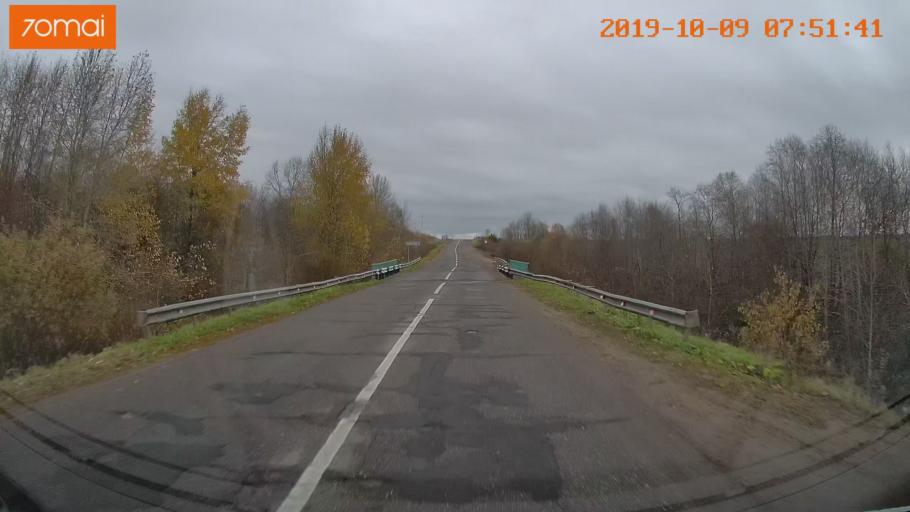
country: RU
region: Jaroslavl
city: Kukoboy
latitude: 58.6850
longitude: 39.8806
